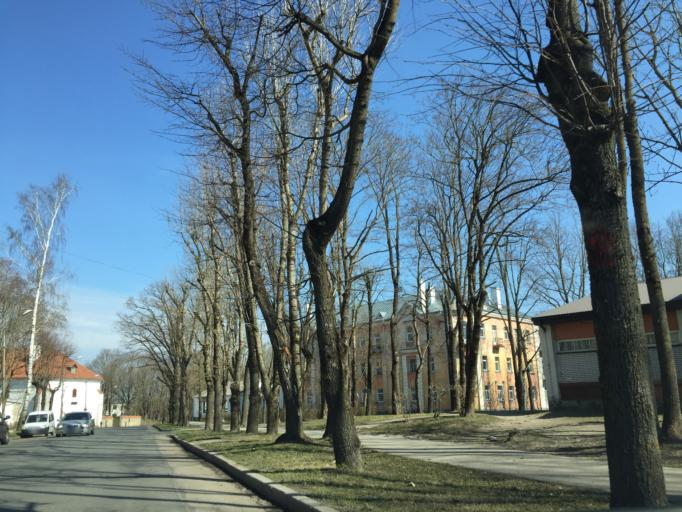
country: EE
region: Ida-Virumaa
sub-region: Narva linn
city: Narva
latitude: 59.3812
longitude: 28.1963
